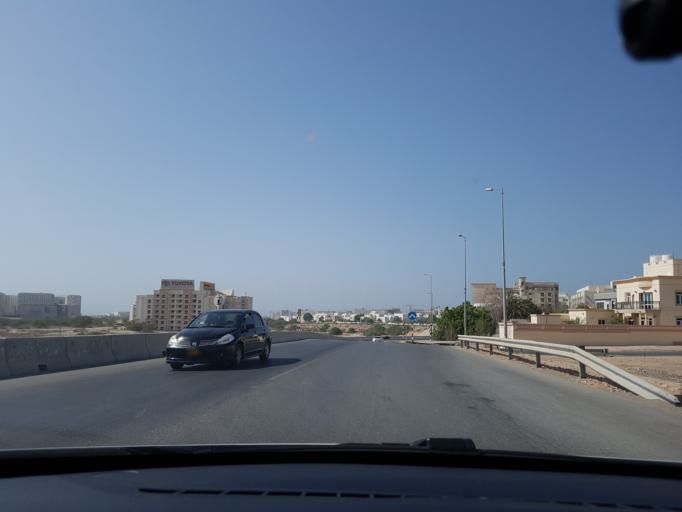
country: OM
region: Muhafazat Masqat
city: Bawshar
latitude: 23.5828
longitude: 58.4220
